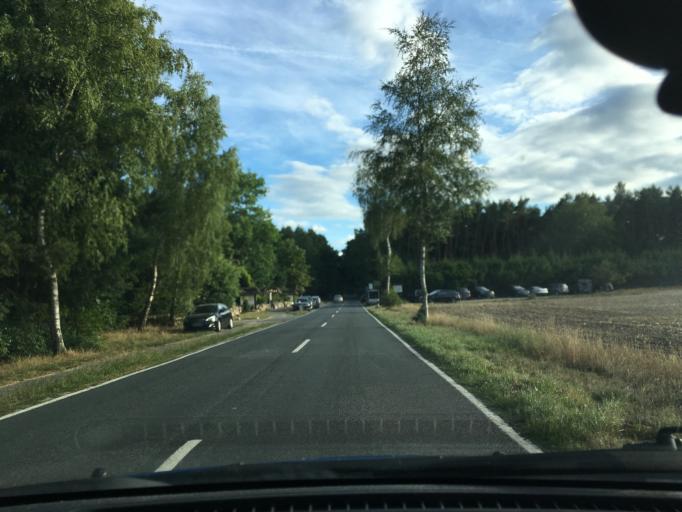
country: DE
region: Lower Saxony
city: Hanstedt
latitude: 53.2460
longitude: 10.0069
